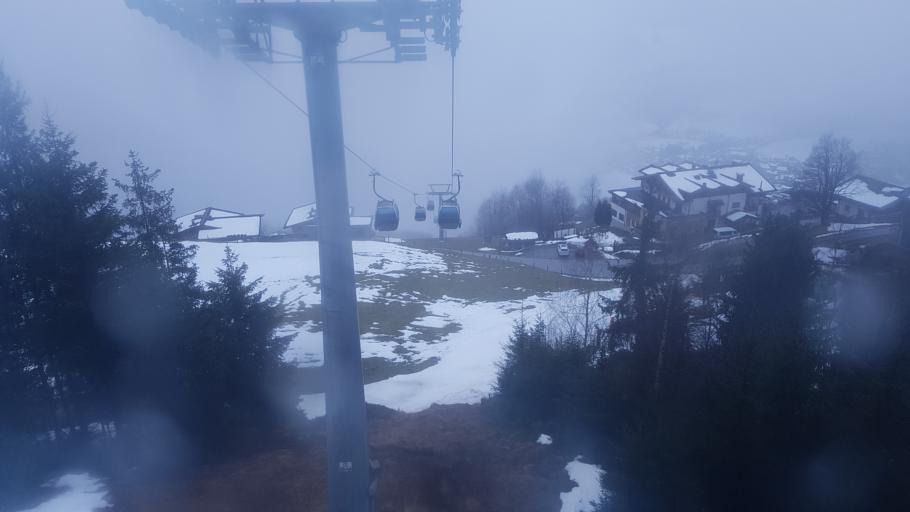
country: AT
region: Salzburg
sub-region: Politischer Bezirk Zell am See
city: Neukirchen am Grossvenediger
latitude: 47.2612
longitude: 12.2809
